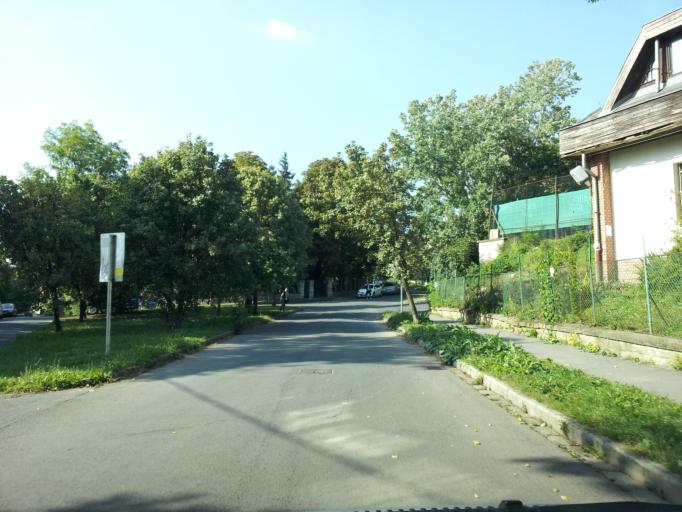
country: HU
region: Budapest
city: Budapest II. keruelet
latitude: 47.5138
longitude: 19.0099
